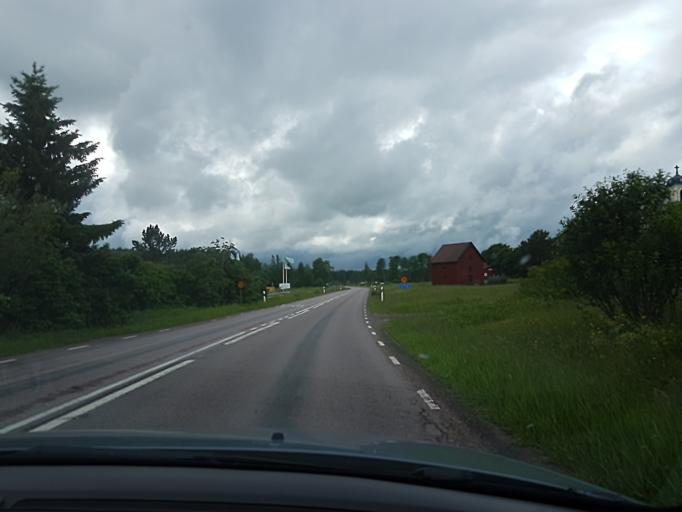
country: SE
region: Uppsala
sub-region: Osthammars Kommun
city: OEsthammar
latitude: 60.2431
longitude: 18.3470
